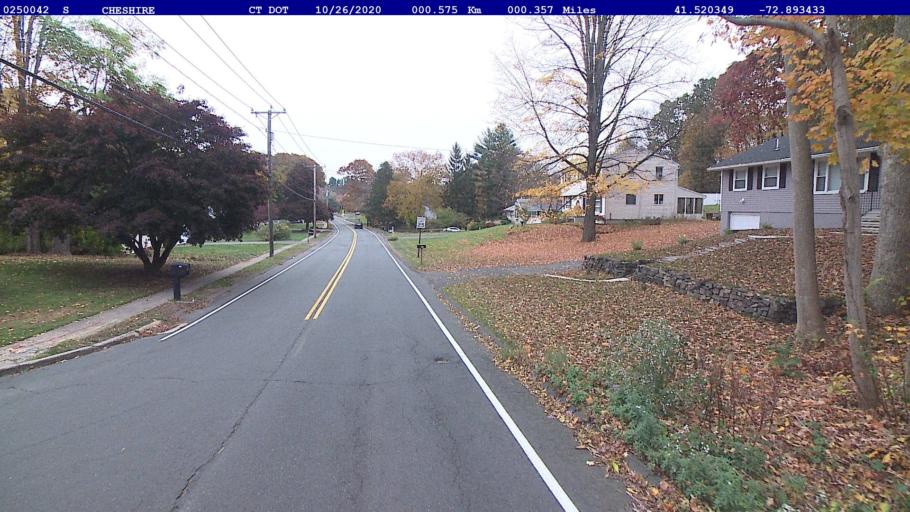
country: US
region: Connecticut
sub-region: New Haven County
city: Cheshire Village
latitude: 41.5204
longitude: -72.8934
